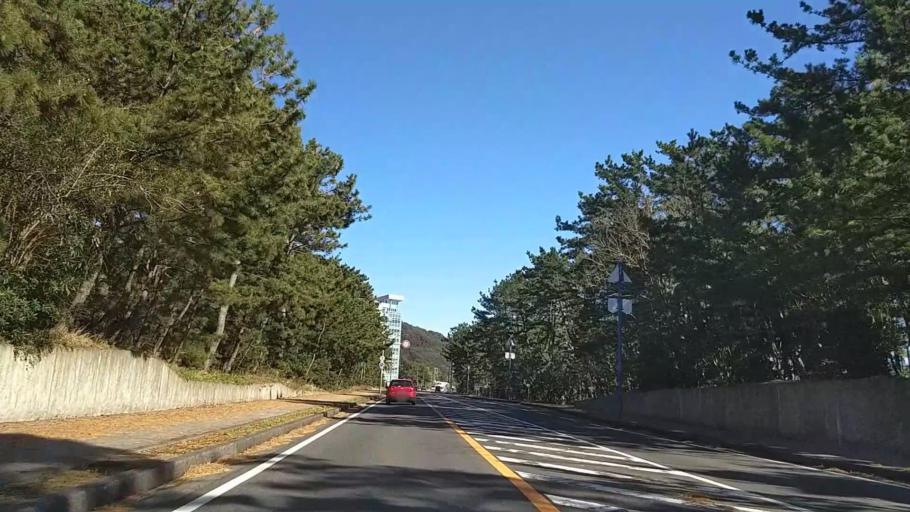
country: JP
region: Chiba
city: Kawaguchi
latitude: 35.1182
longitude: 140.1232
